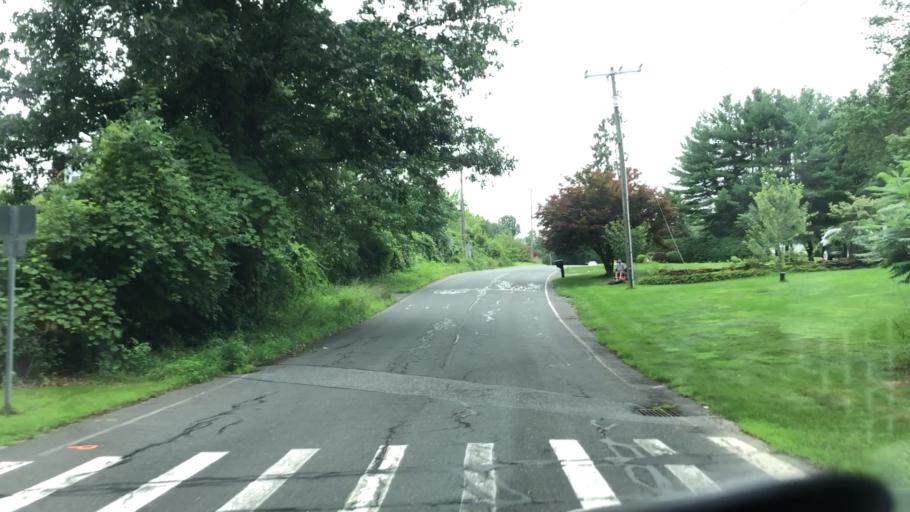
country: US
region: Massachusetts
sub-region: Hampshire County
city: Easthampton
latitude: 42.2510
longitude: -72.6954
